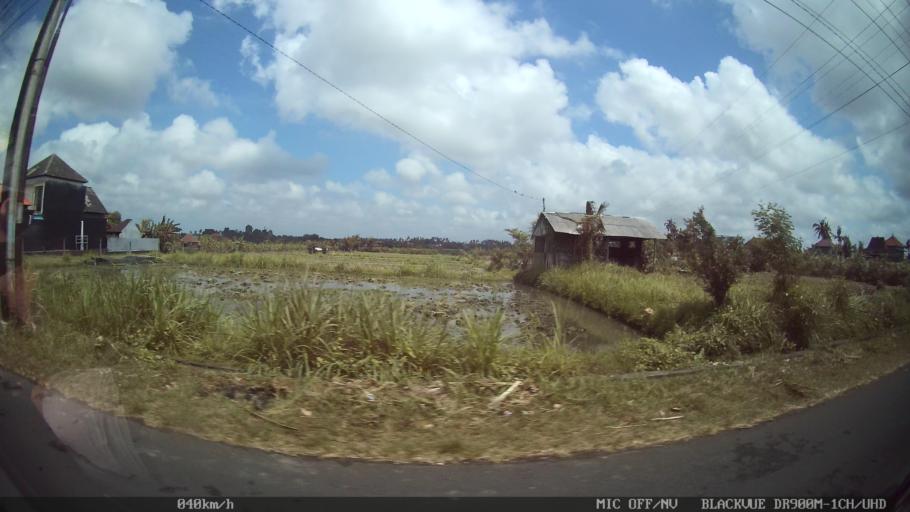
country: ID
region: Bali
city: Banjar Desa
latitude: -8.5783
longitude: 115.2877
